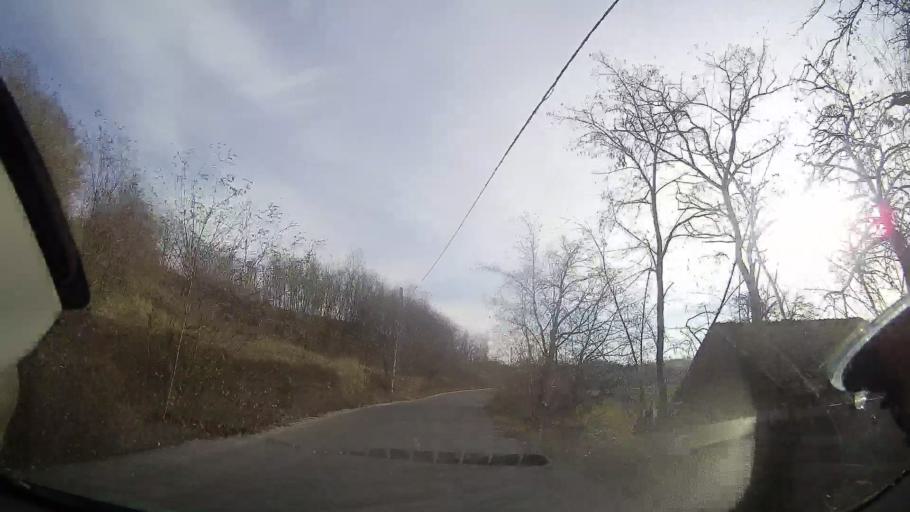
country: RO
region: Bihor
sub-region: Comuna Sarbi
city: Burzuc
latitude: 47.1330
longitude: 22.1863
